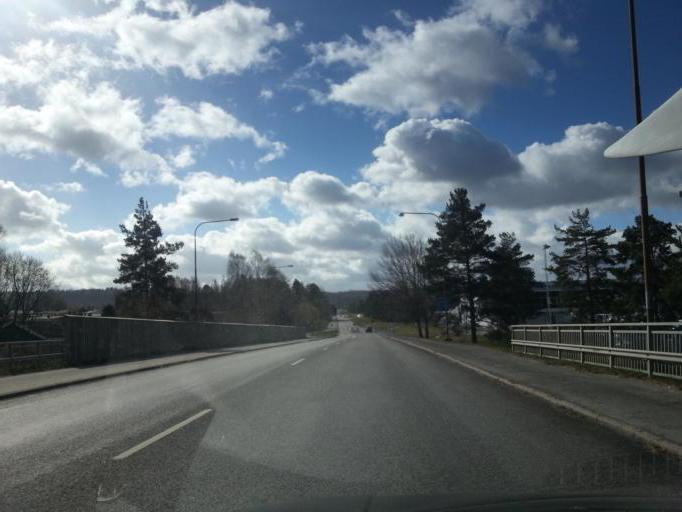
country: SE
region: Joenkoeping
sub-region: Jonkopings Kommun
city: Jonkoping
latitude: 57.7585
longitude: 14.1686
